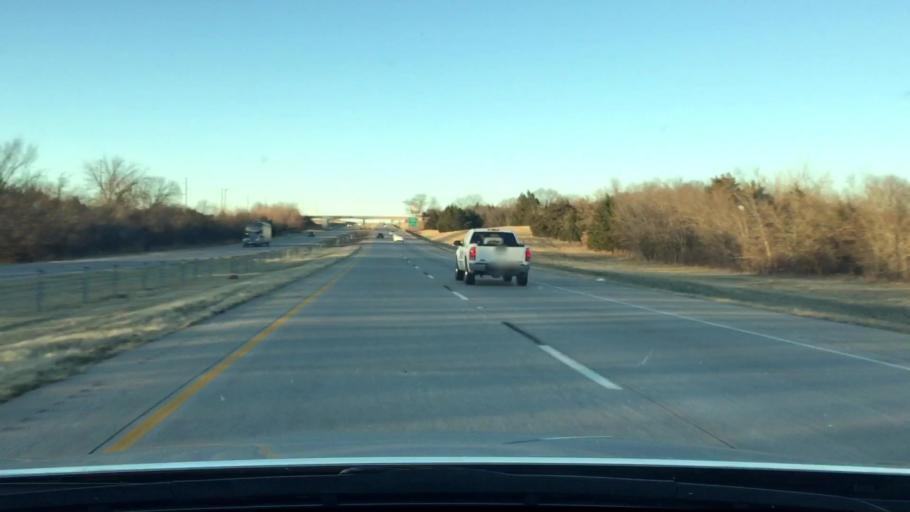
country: US
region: Oklahoma
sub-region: Love County
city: Marietta
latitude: 33.8785
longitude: -97.1343
